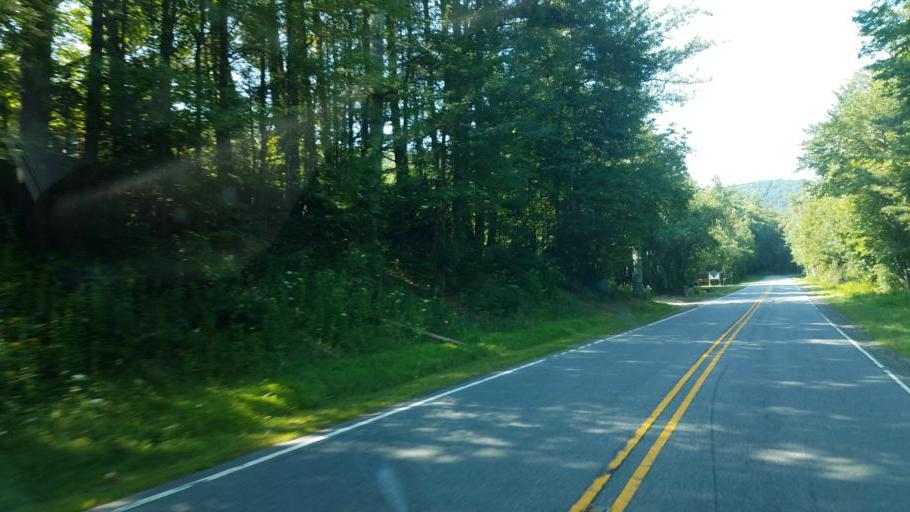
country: US
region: North Carolina
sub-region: Avery County
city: Newland
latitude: 35.9890
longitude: -81.8920
